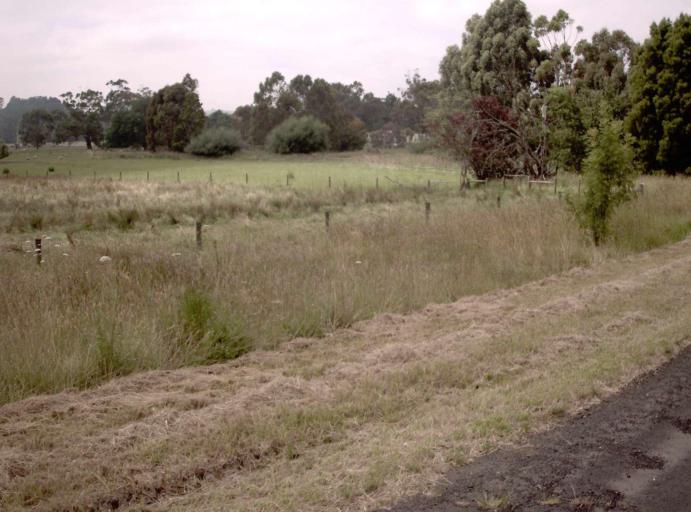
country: AU
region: Victoria
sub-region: Baw Baw
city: Warragul
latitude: -38.4029
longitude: 146.0712
